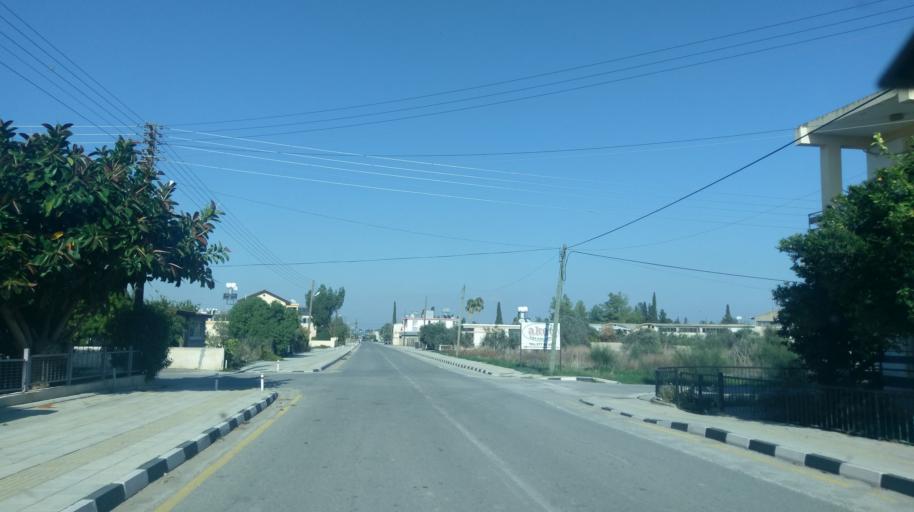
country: CY
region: Larnaka
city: Pergamos
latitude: 35.1068
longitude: 33.6766
